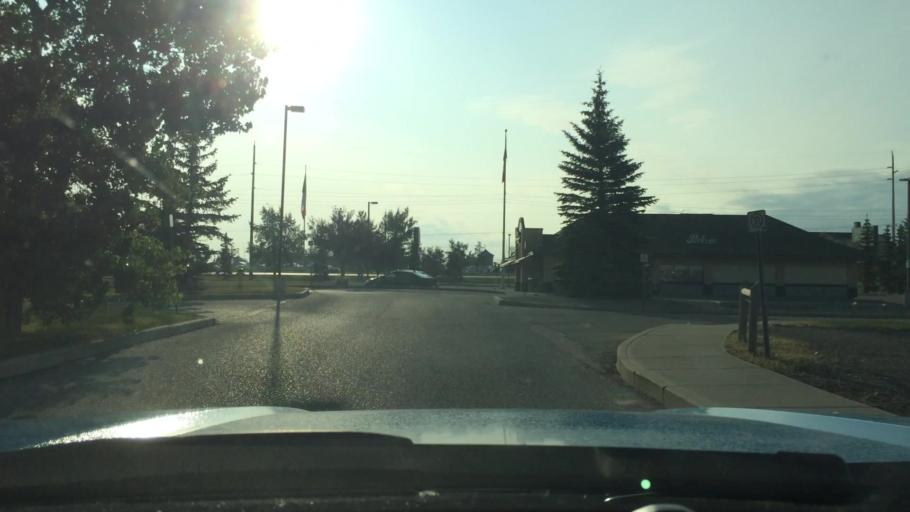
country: CA
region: Alberta
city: Calgary
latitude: 51.0805
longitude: -114.0040
